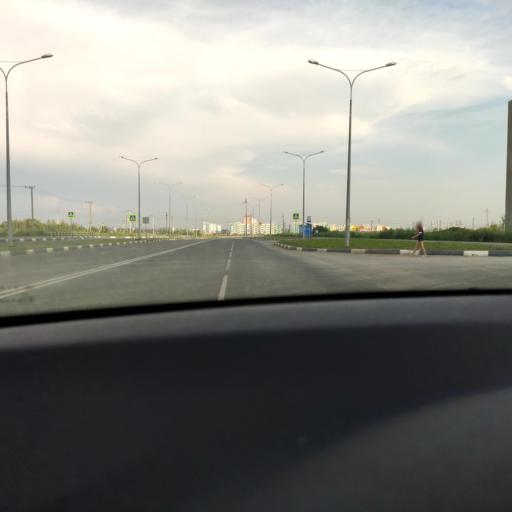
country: RU
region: Samara
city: Samara
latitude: 53.1450
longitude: 50.0761
